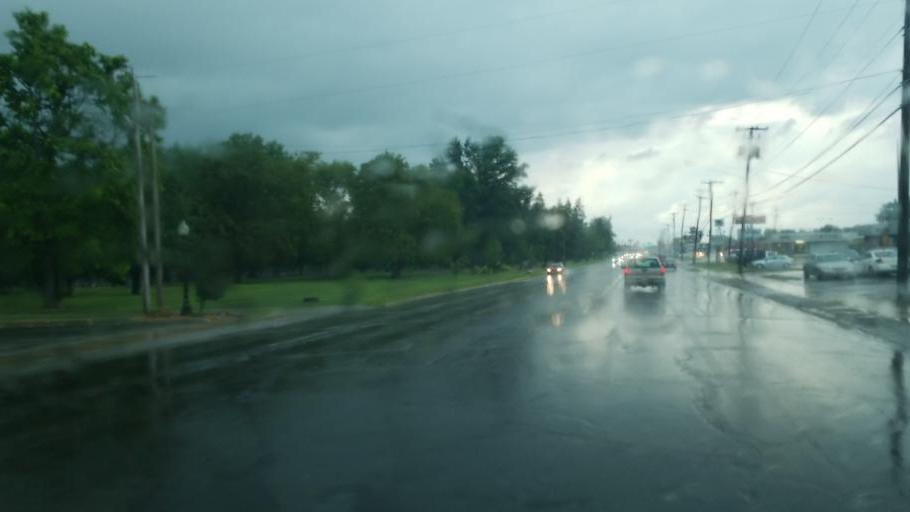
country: US
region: Ohio
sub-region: Trumbull County
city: Churchill
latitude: 41.1420
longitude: -80.6655
